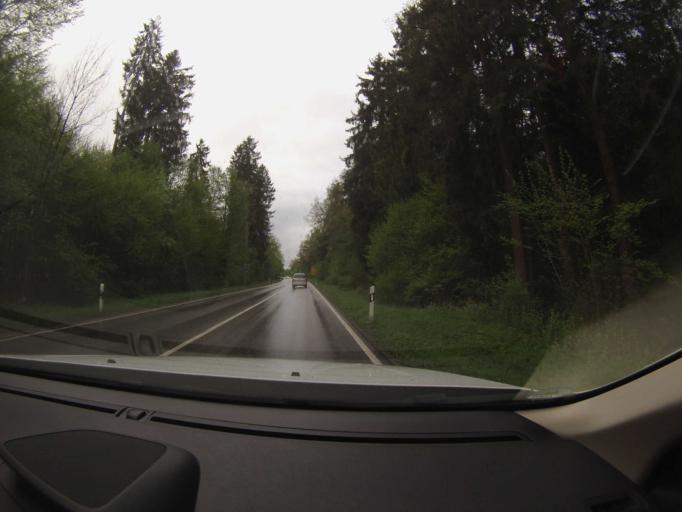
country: DE
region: Bavaria
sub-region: Upper Bavaria
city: Sauerlach
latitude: 48.0016
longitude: 11.6401
